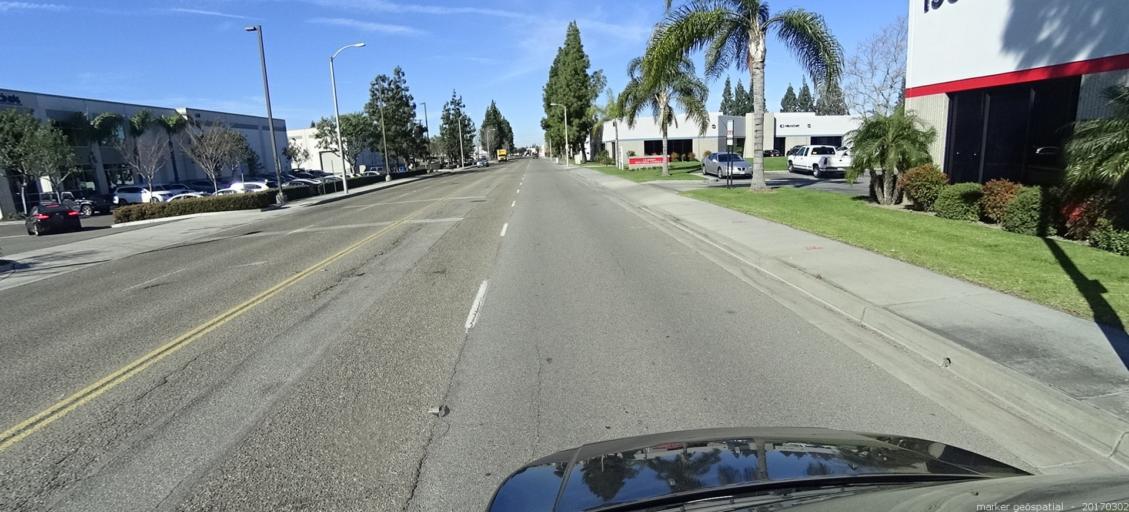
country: US
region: California
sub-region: Orange County
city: Yorba Linda
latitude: 33.8621
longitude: -117.8214
